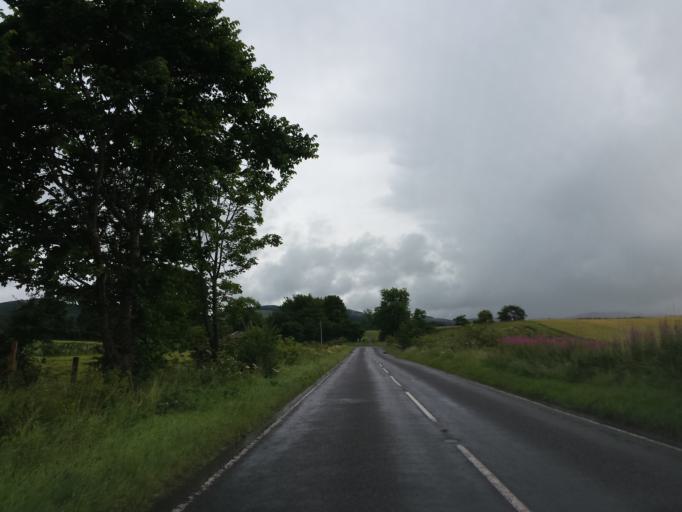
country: GB
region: Scotland
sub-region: Perth and Kinross
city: Errol
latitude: 56.3412
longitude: -3.1782
